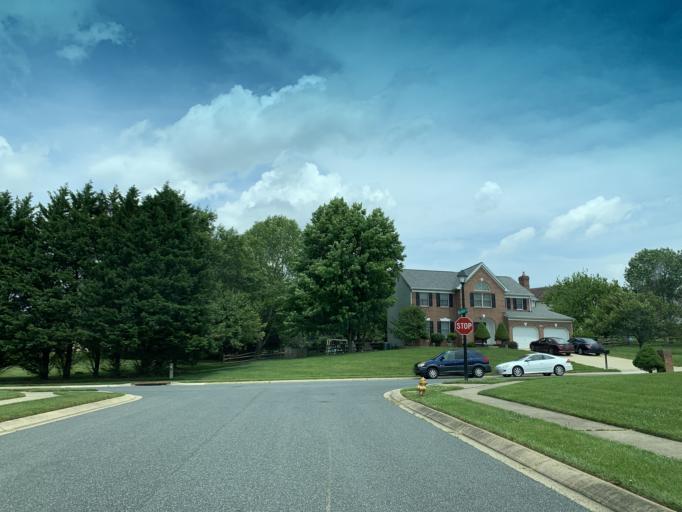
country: US
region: Maryland
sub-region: Harford County
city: South Bel Air
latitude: 39.5540
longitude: -76.3367
